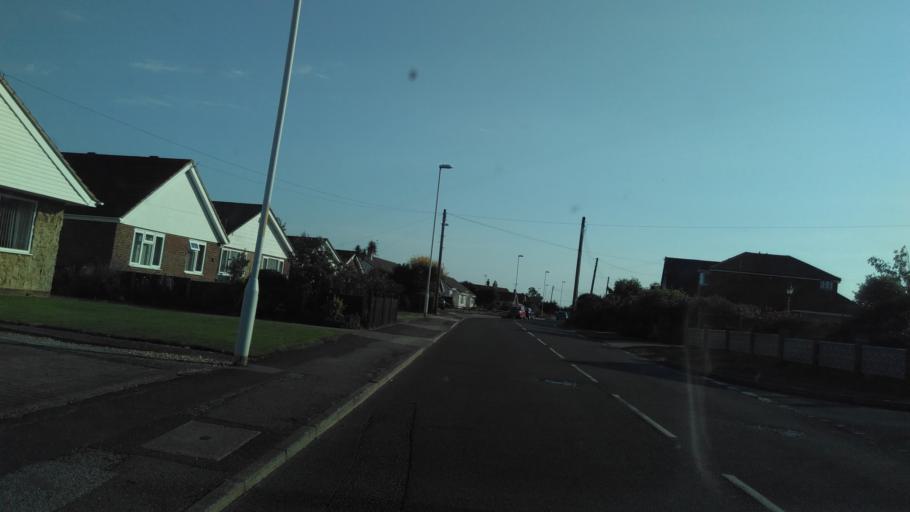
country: GB
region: England
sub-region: Kent
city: Whitstable
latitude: 51.3455
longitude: 1.0019
